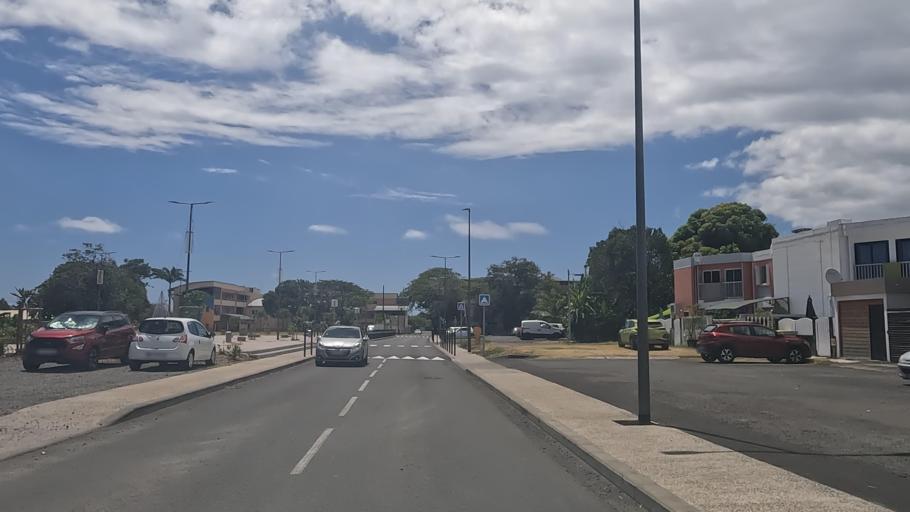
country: RE
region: Reunion
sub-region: Reunion
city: Saint-Benoit
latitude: -21.0309
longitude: 55.7131
